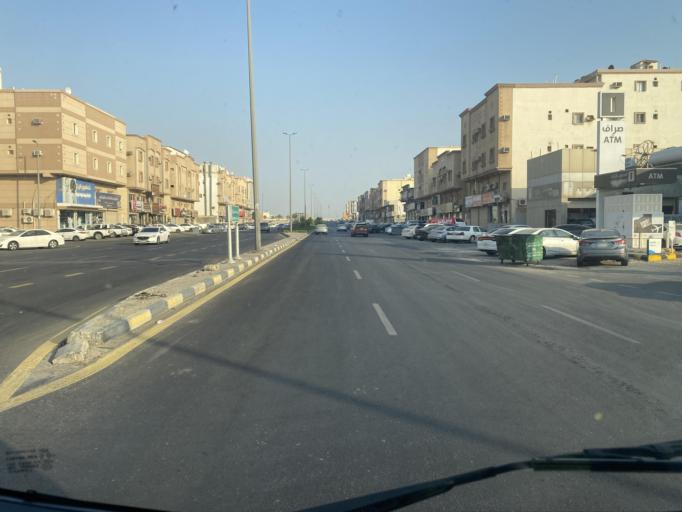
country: SA
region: Eastern Province
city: Dhahran
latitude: 26.3546
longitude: 50.0479
